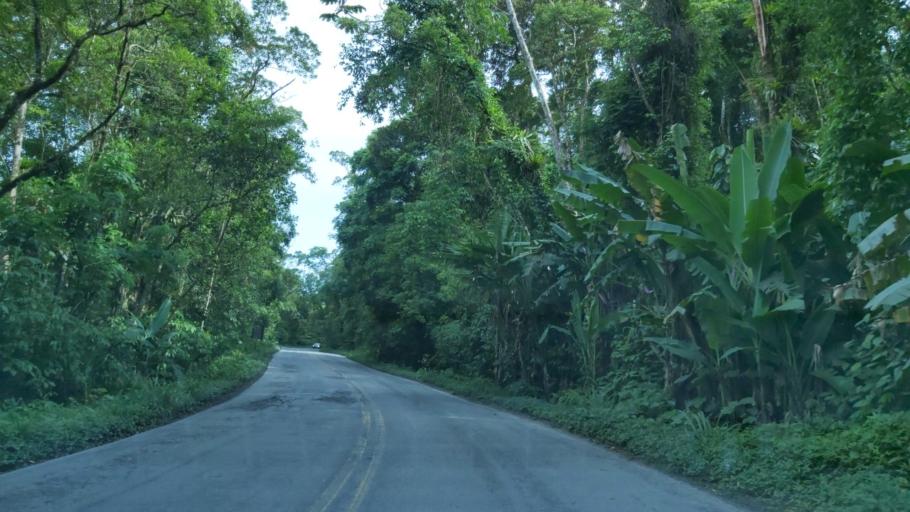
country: BR
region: Sao Paulo
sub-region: Miracatu
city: Miracatu
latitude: -24.0396
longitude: -47.5668
